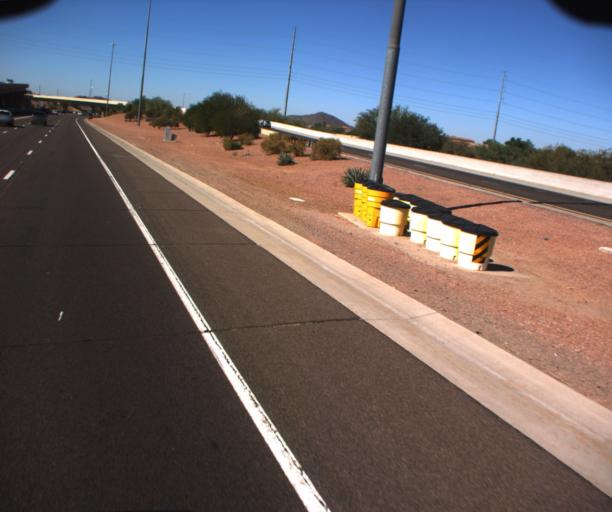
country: US
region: Arizona
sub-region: Maricopa County
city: Paradise Valley
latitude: 33.6727
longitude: -111.9935
